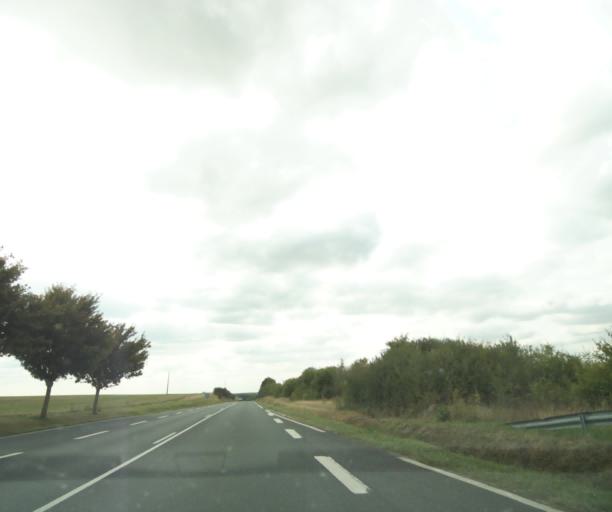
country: FR
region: Centre
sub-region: Departement de l'Indre
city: Buzancais
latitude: 46.8800
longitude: 1.4393
